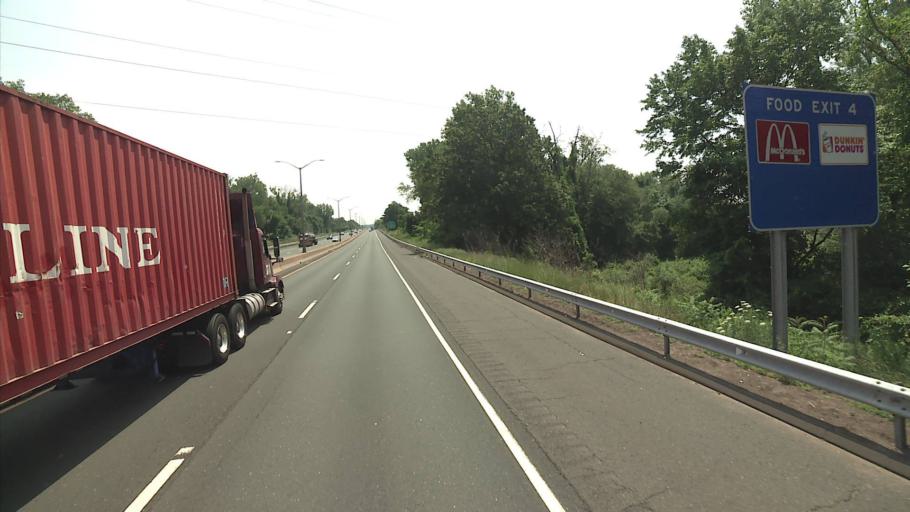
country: US
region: Connecticut
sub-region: Hartford County
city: South Windsor
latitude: 41.8096
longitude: -72.6312
